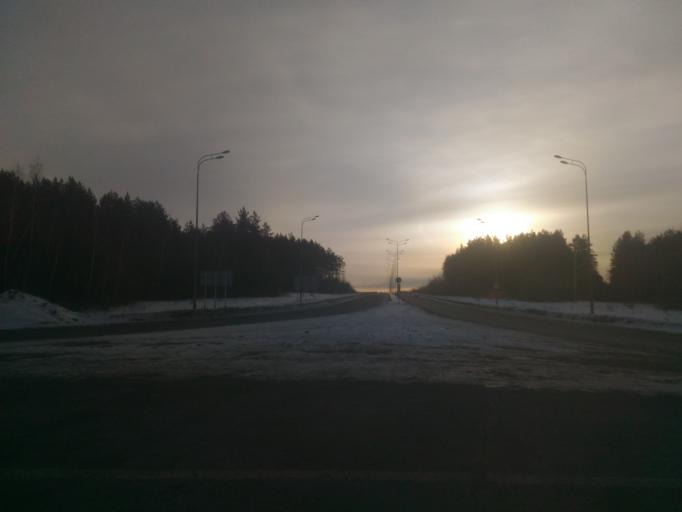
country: RU
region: Ulyanovsk
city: Isheyevka
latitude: 54.3752
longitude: 48.3098
